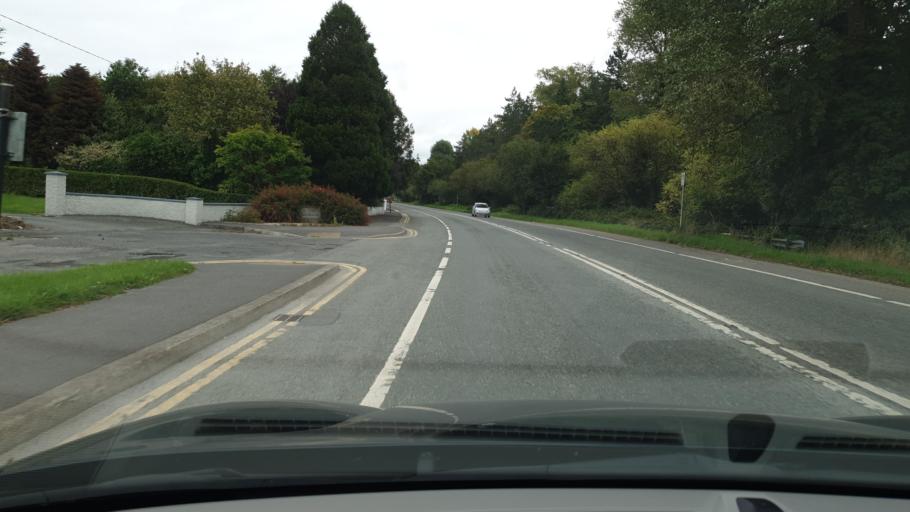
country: IE
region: Leinster
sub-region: Kildare
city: Maynooth
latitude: 53.3815
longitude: -6.6061
